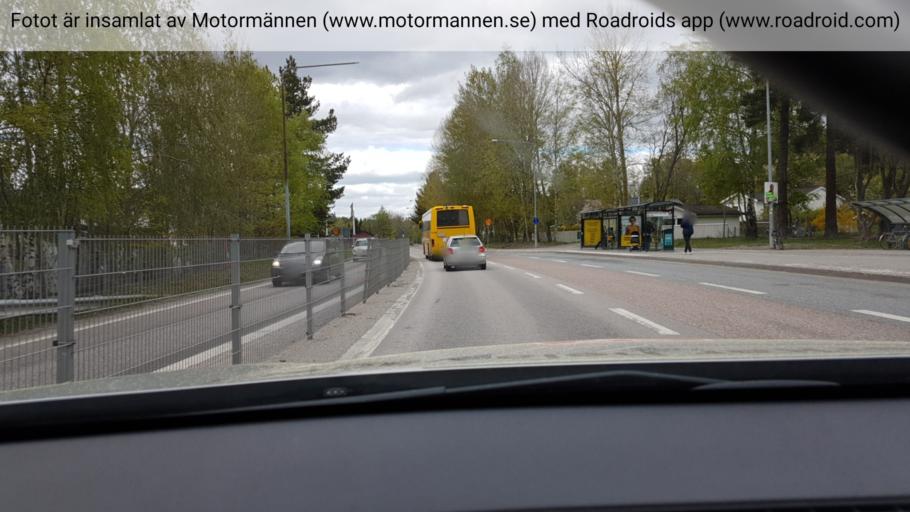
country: SE
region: Stockholm
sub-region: Tyreso Kommun
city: Bollmora
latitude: 59.2241
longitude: 18.2024
